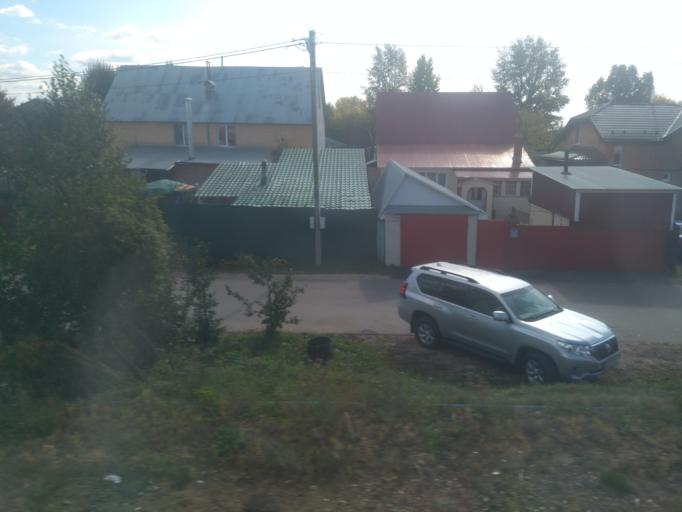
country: RU
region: Tatarstan
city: Verkhniy Uslon
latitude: 55.8013
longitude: 49.0218
